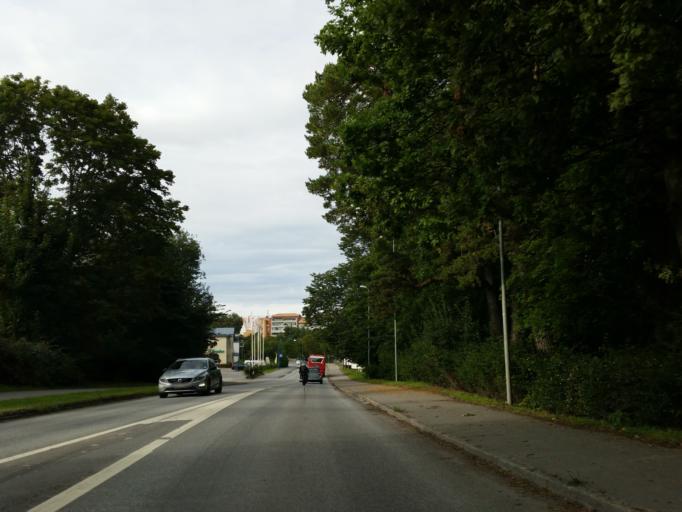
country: SE
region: Stockholm
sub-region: Sollentuna Kommun
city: Sollentuna
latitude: 59.4390
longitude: 17.9506
